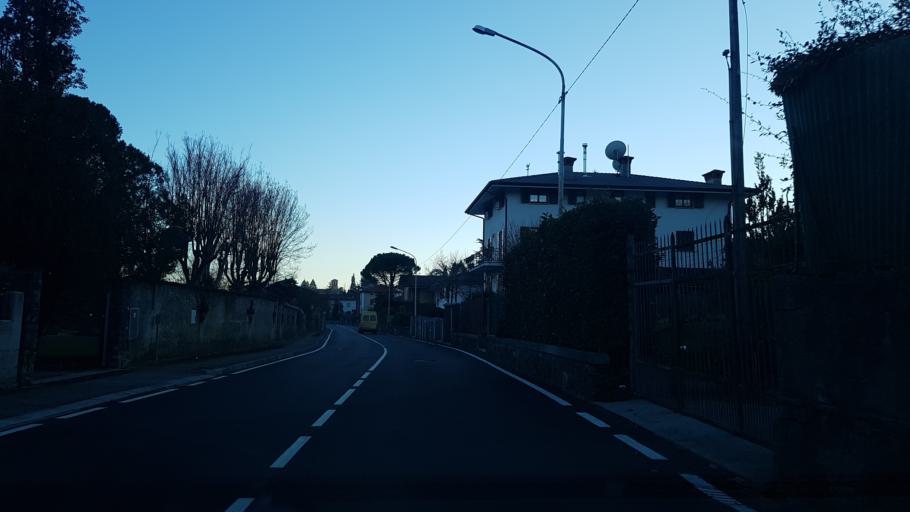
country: IT
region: Friuli Venezia Giulia
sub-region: Provincia di Udine
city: Tarcento
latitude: 46.2220
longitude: 13.2214
